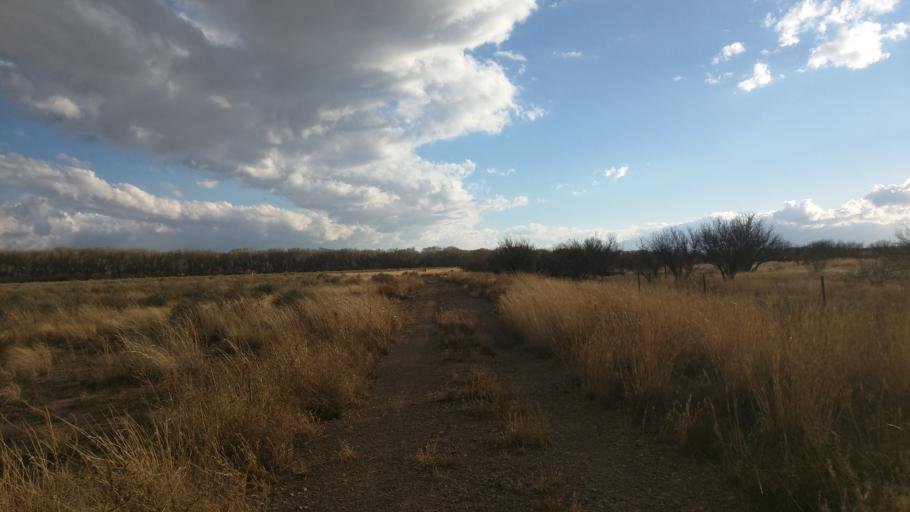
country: US
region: Arizona
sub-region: Cochise County
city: Sierra Vista Southeast
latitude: 31.3706
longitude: -110.1223
